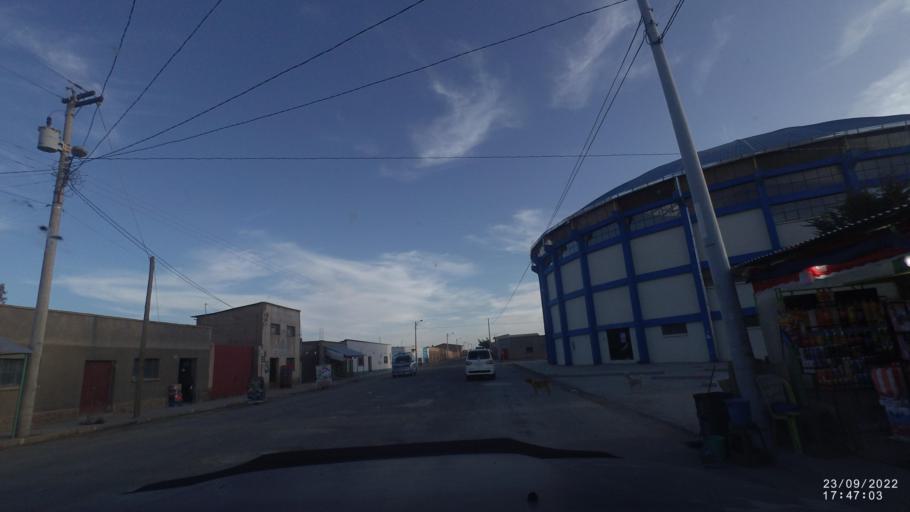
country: BO
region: Oruro
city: Challapata
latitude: -19.0168
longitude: -66.7773
